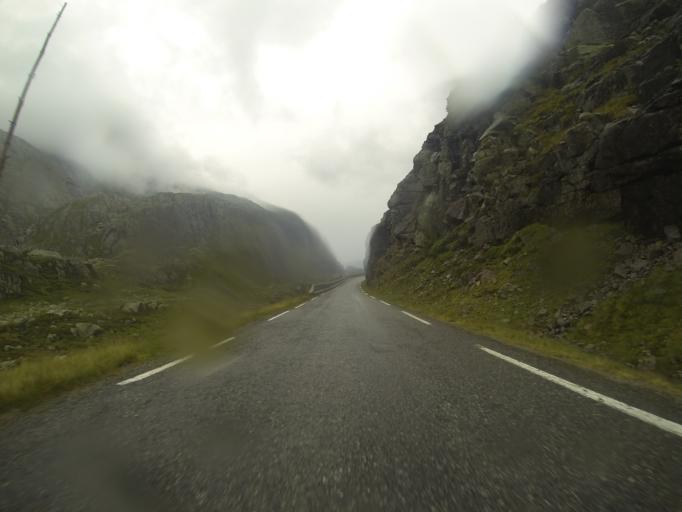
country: NO
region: Hordaland
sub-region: Odda
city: Odda
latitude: 59.7623
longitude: 6.7221
